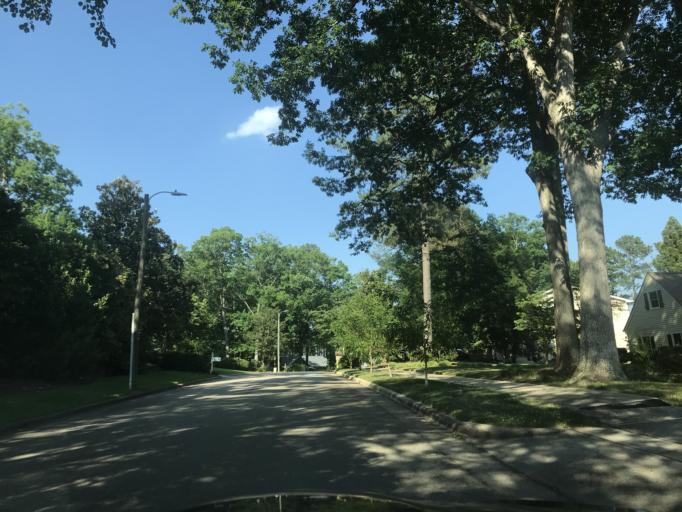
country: US
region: North Carolina
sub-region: Wake County
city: West Raleigh
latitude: 35.8731
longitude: -78.6123
